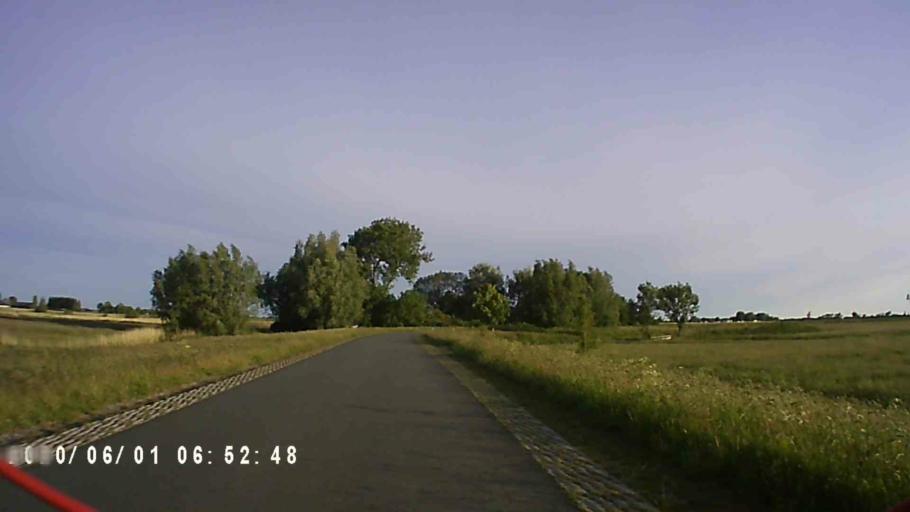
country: NL
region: Friesland
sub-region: Gemeente Kollumerland en Nieuwkruisland
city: Kollum
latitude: 53.3099
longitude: 6.1298
